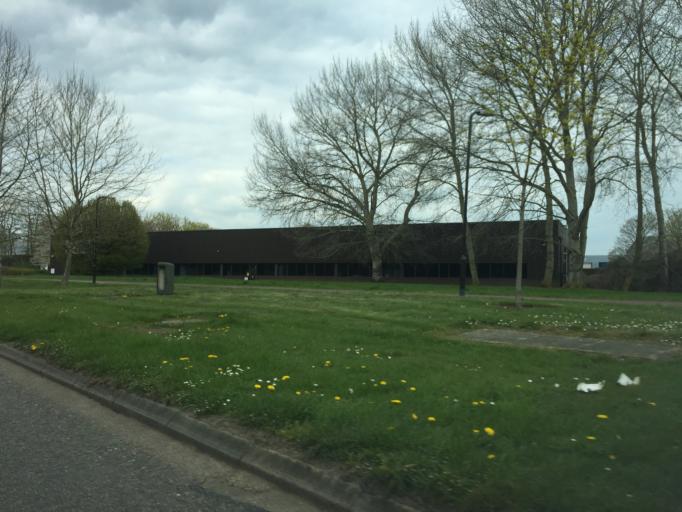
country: GB
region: England
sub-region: Milton Keynes
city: Newport Pagnell
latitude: 52.0756
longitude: -0.7454
